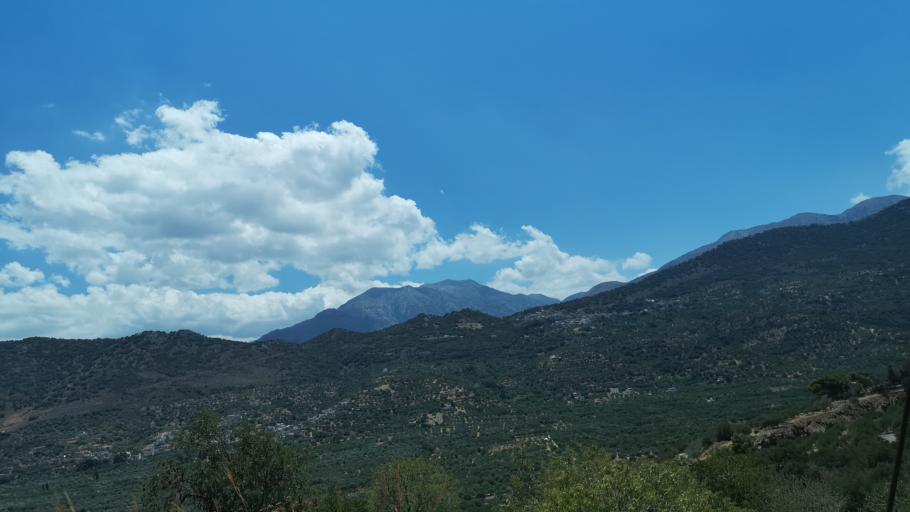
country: GR
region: Crete
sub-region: Nomos Lasithiou
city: Neapoli
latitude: 35.2514
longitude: 25.6313
